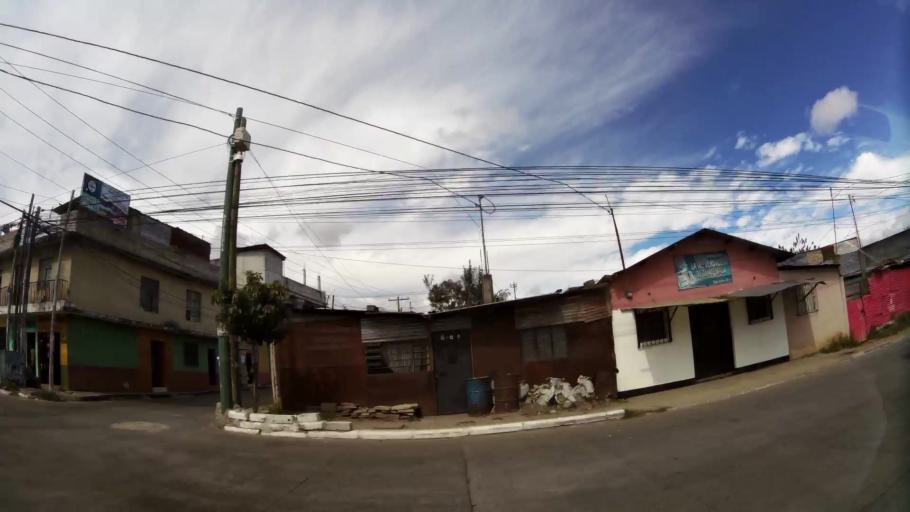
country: GT
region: Guatemala
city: Mixco
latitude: 14.6371
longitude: -90.5811
